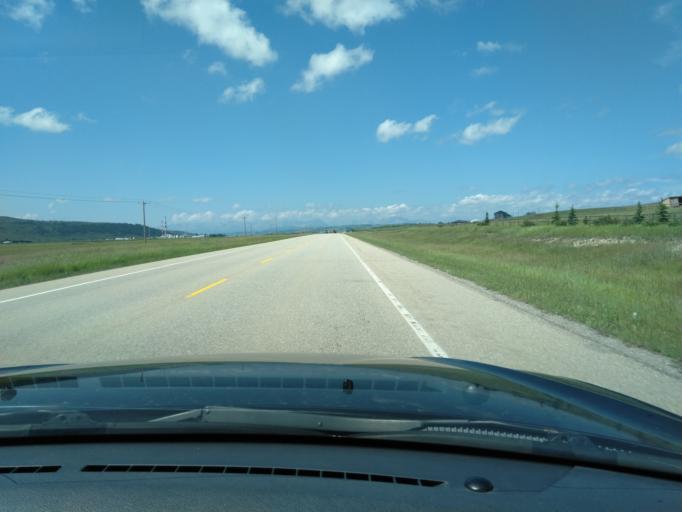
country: CA
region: Alberta
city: Cochrane
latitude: 51.2247
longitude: -114.6364
